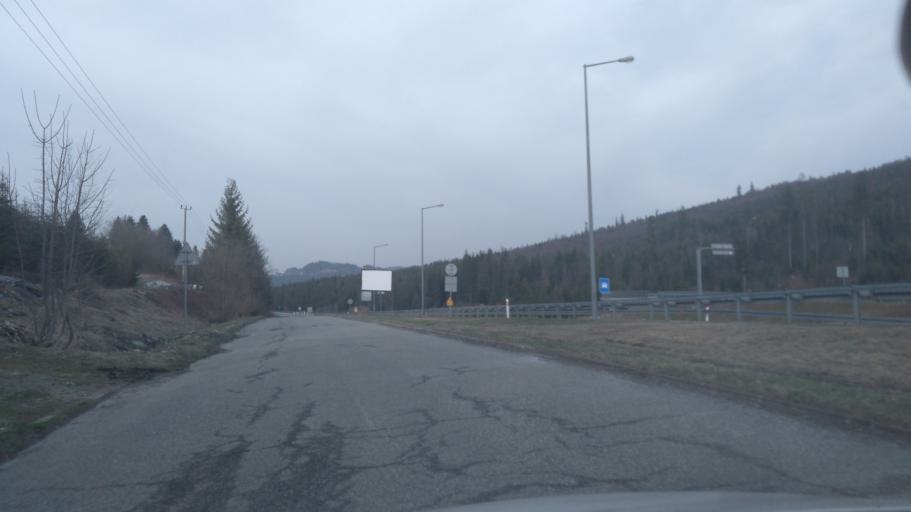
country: PL
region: Silesian Voivodeship
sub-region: Powiat zywiecki
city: Laliki
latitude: 49.5127
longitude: 18.9783
